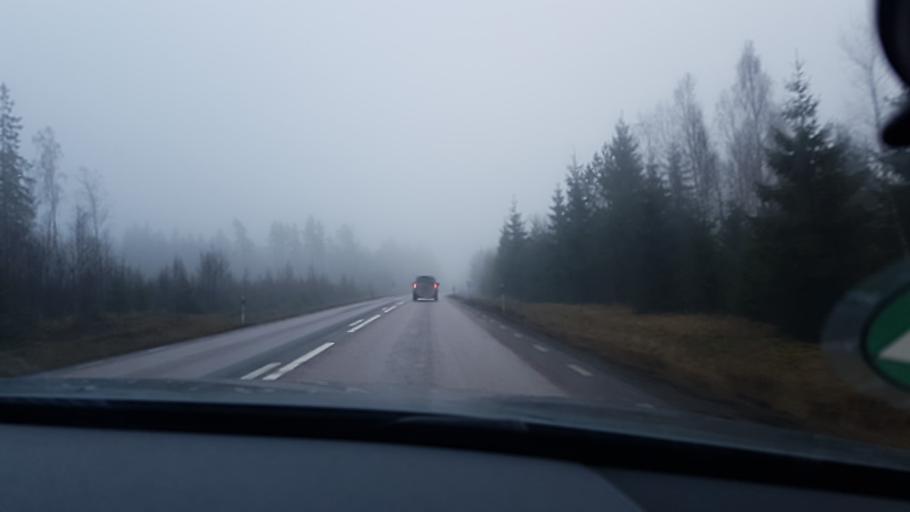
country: SE
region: Vaermland
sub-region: Kristinehamns Kommun
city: Bjorneborg
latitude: 59.2542
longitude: 14.1753
